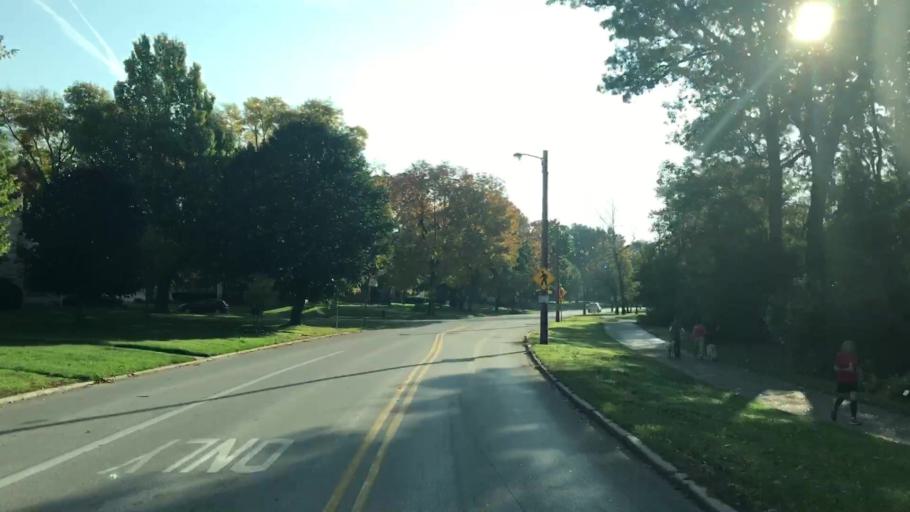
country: US
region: Wisconsin
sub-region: Milwaukee County
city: Wauwatosa
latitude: 43.0567
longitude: -88.0271
